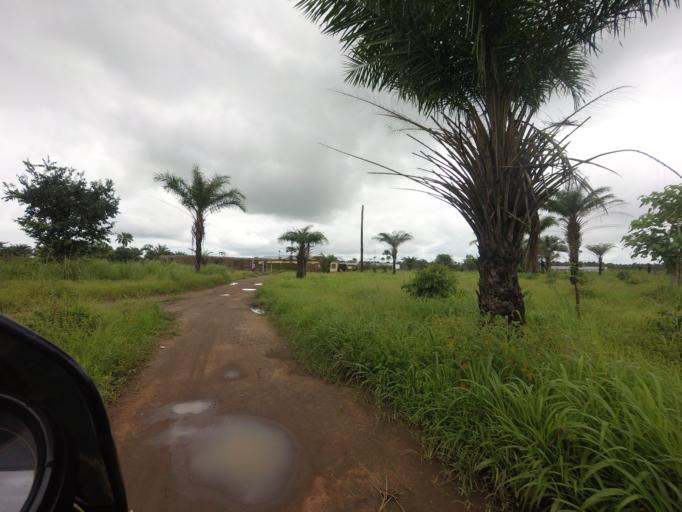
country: SL
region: Northern Province
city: Kambia
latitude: 9.1308
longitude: -12.9042
